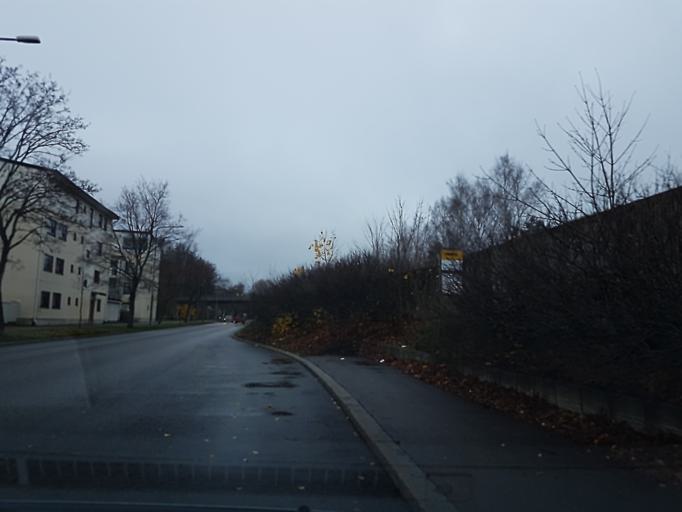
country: FI
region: Uusimaa
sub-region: Helsinki
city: Vantaa
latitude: 60.2313
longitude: 25.0761
